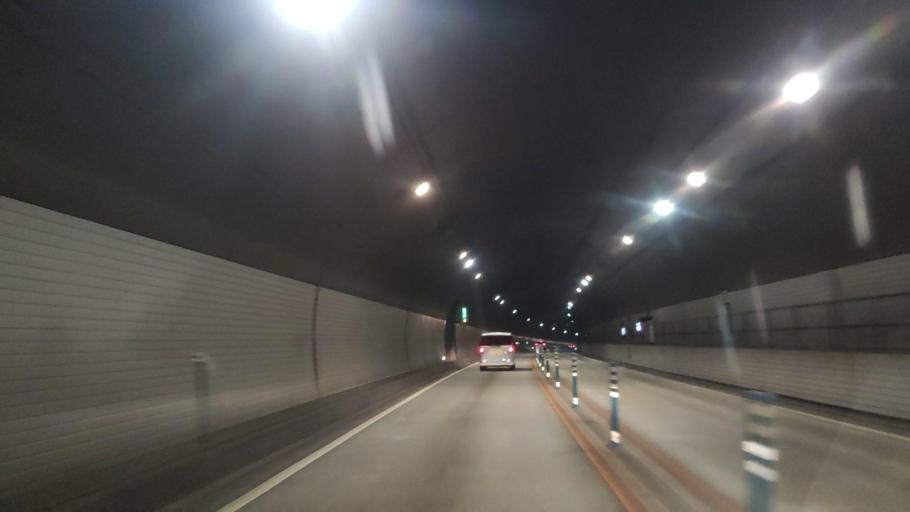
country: JP
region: Gifu
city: Takayama
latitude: 36.1729
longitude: 137.2249
